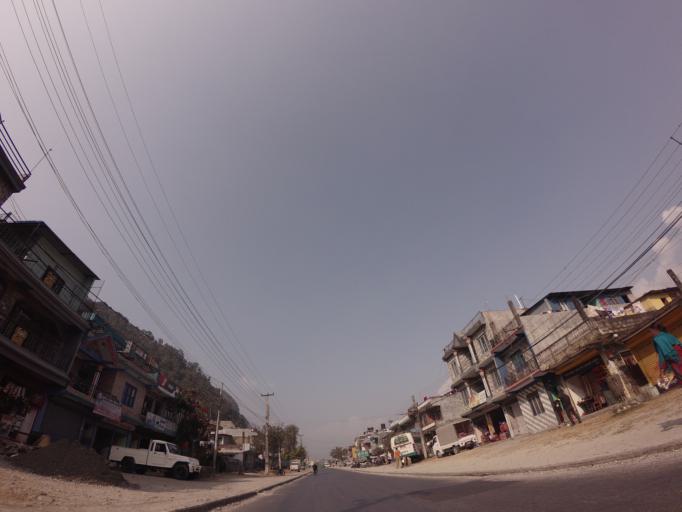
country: NP
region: Western Region
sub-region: Gandaki Zone
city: Pokhara
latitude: 28.2458
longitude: 83.9803
